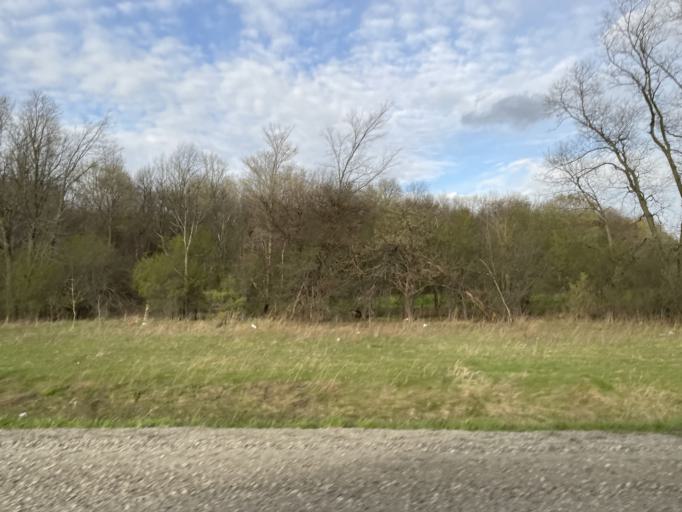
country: CA
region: Ontario
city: Waterloo
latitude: 43.4768
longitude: -80.4029
